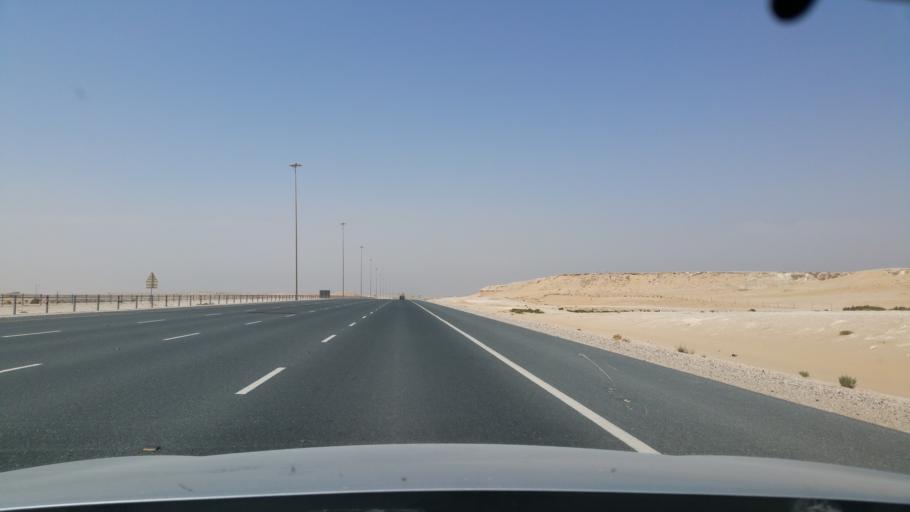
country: QA
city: Umm Bab
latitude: 24.8712
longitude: 50.9146
